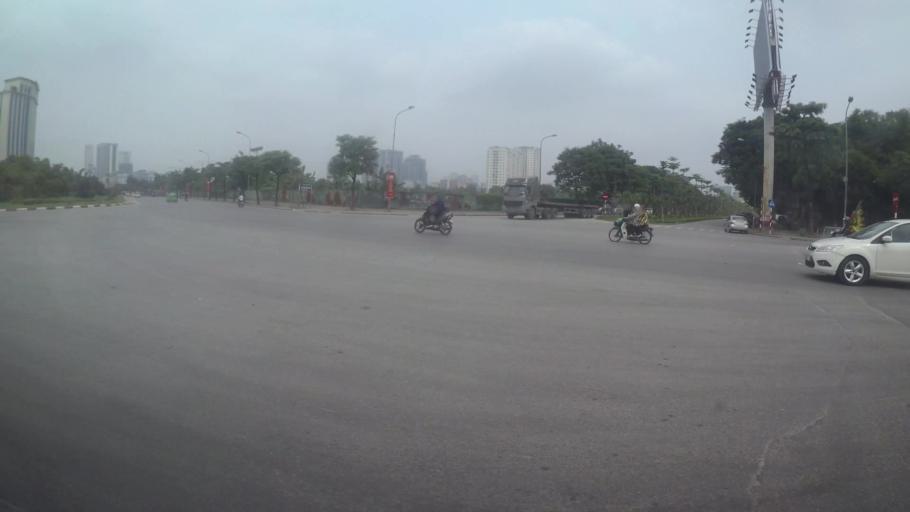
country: VN
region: Ha Noi
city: Cau Dien
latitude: 21.0237
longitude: 105.7669
